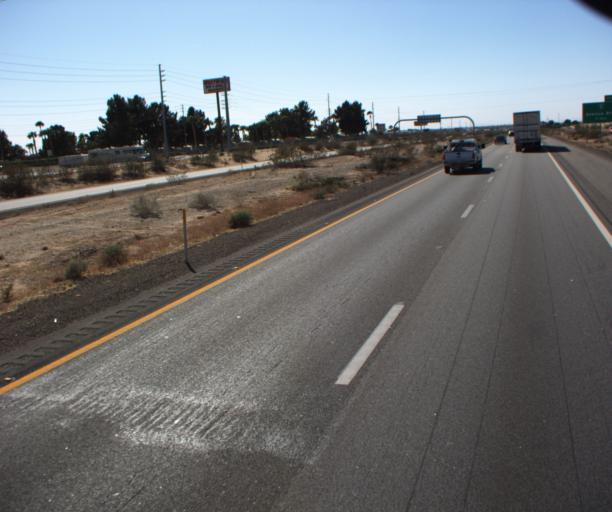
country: US
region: Arizona
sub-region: Yuma County
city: Fortuna Foothills
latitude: 32.6708
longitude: -114.4597
